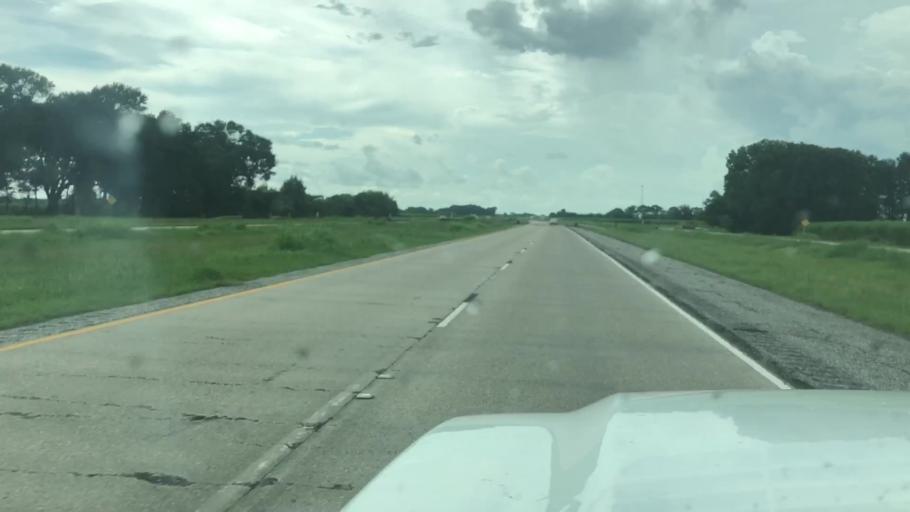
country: US
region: Louisiana
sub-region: Saint Mary Parish
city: Baldwin
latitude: 29.8566
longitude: -91.6103
